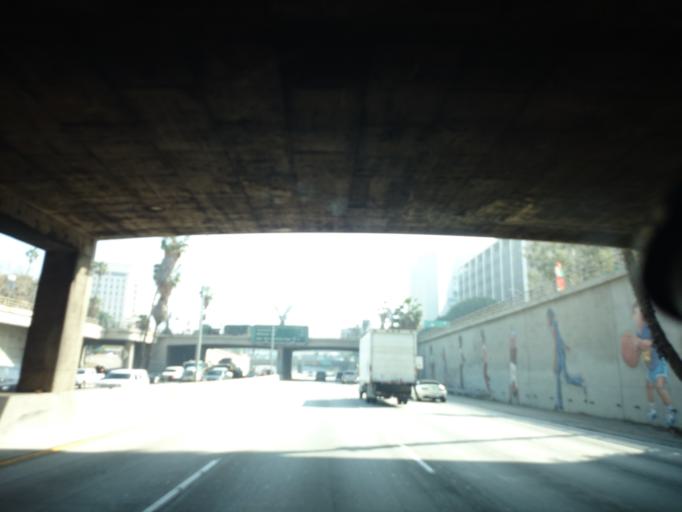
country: US
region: California
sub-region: Los Angeles County
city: Los Angeles
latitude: 34.0557
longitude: -118.2404
